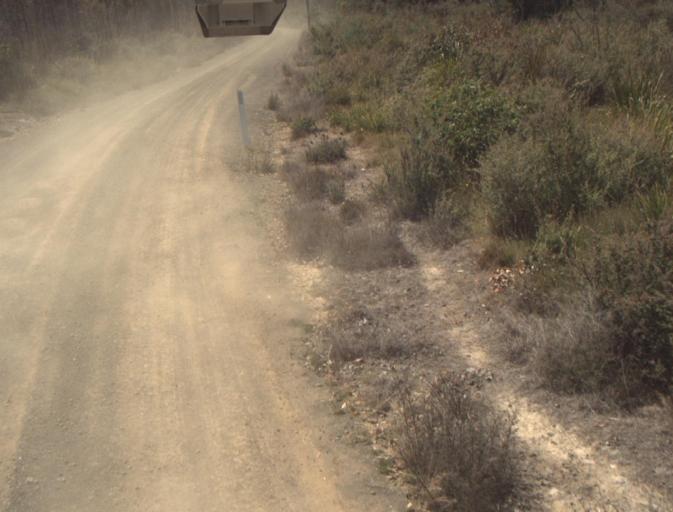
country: AU
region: Tasmania
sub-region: Launceston
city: Mayfield
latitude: -41.2793
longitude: 147.0959
